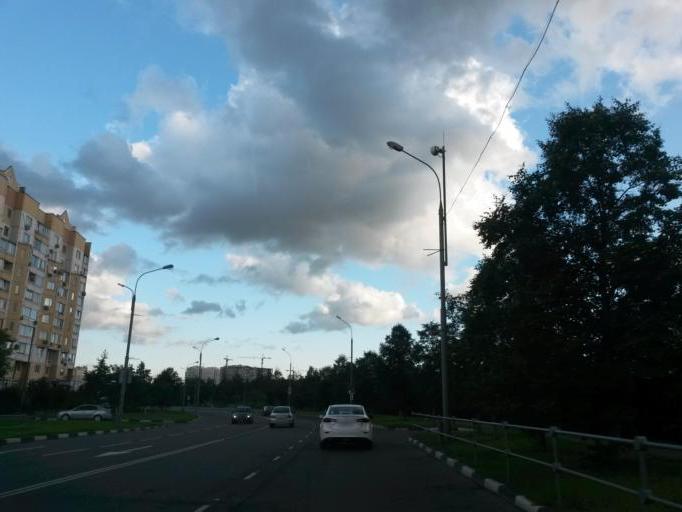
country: RU
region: Moscow
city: Zhulebino
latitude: 55.6842
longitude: 37.8419
